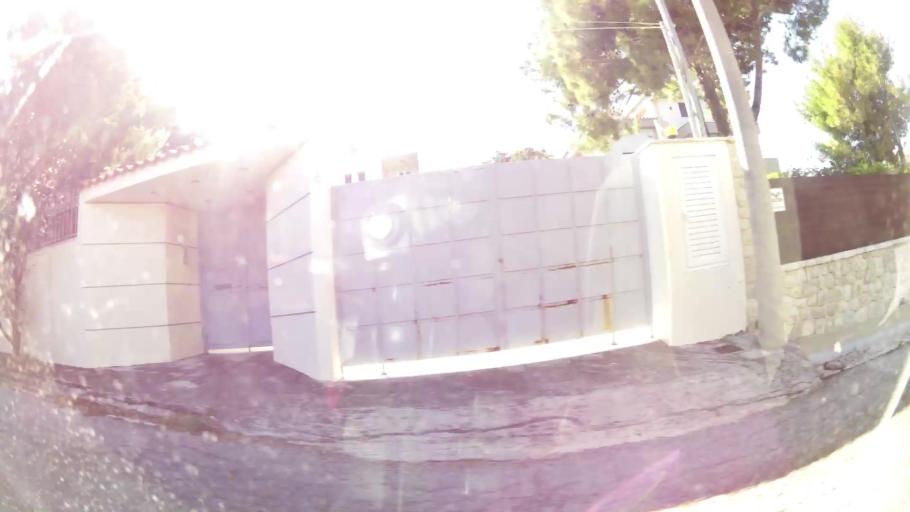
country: GR
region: Attica
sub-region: Nomarchia Anatolikis Attikis
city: Dhrafi
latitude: 38.0197
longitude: 23.9073
